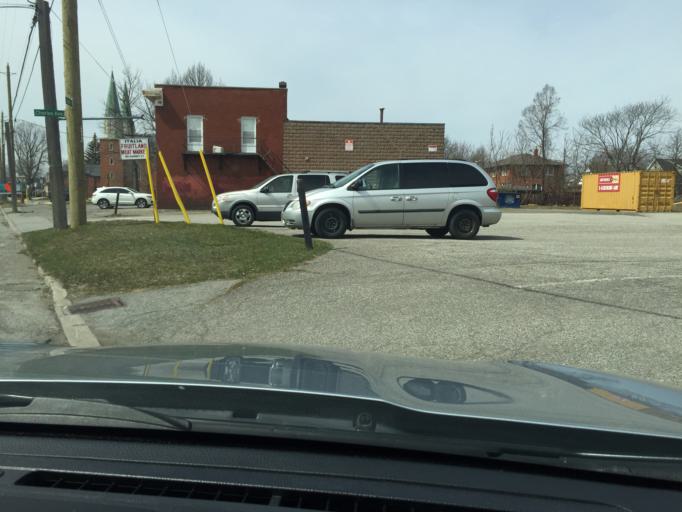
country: CA
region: Ontario
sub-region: Regional Municipality of Niagara
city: St. Catharines
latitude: 43.1793
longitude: -79.2225
